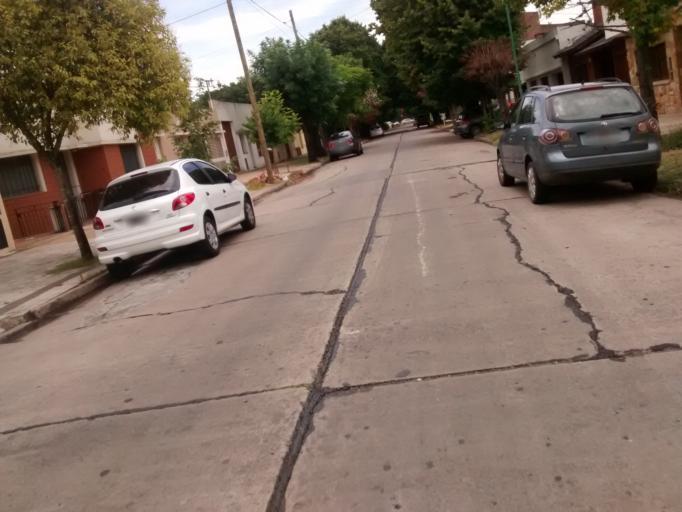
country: AR
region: Buenos Aires
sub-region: Partido de La Plata
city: La Plata
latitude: -34.9000
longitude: -57.9721
